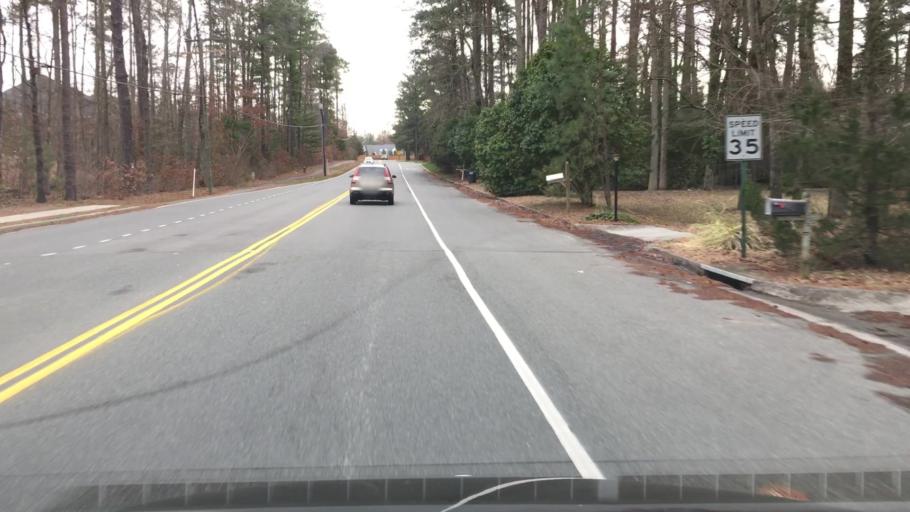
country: US
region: Virginia
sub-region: Henrico County
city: Tuckahoe
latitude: 37.5921
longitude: -77.5977
